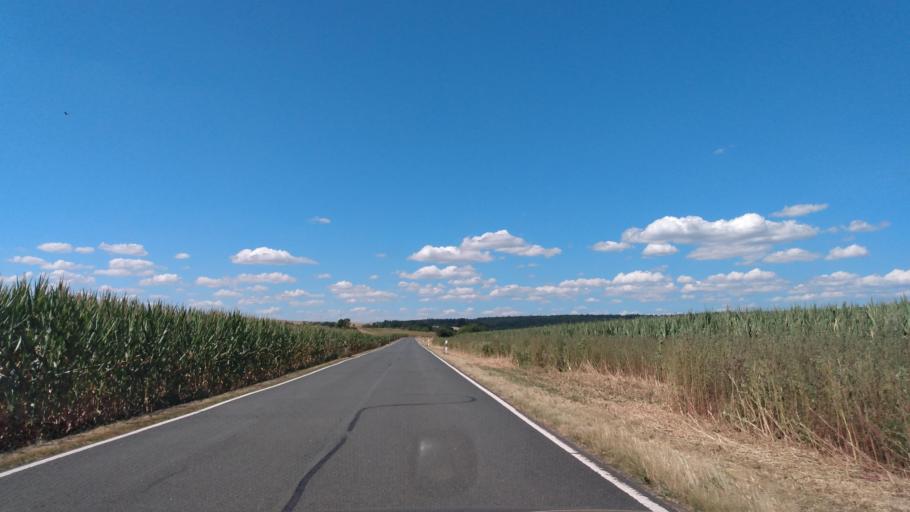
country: DE
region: Rheinland-Pfalz
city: Oberkail
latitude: 50.0263
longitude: 6.6906
